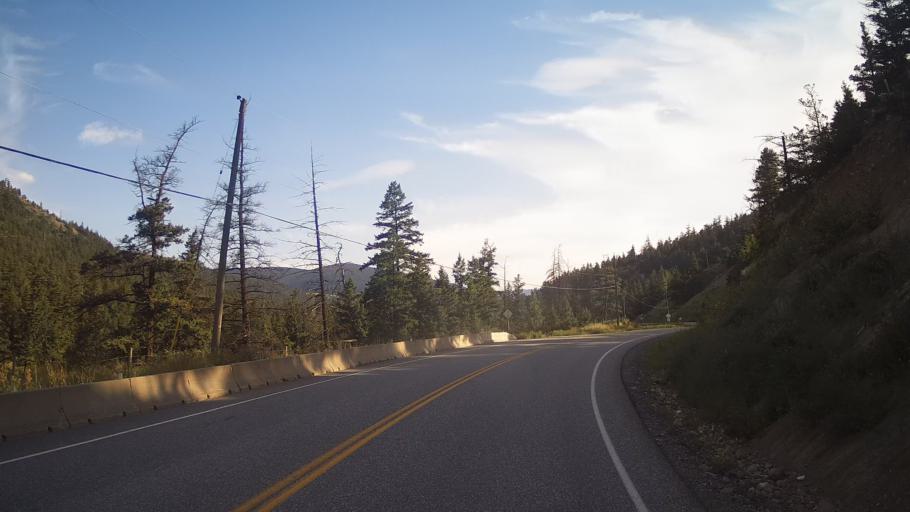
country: CA
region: British Columbia
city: Cache Creek
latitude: 50.8634
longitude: -121.5274
